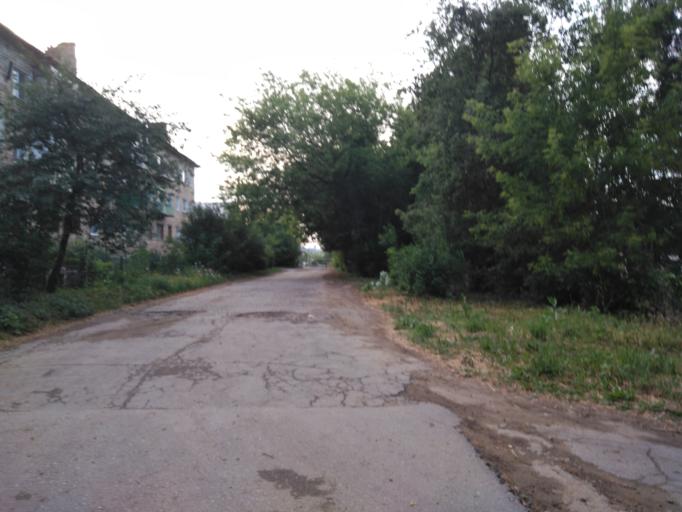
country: RU
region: Tula
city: Lomintsevskiy
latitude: 53.9362
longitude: 37.6240
